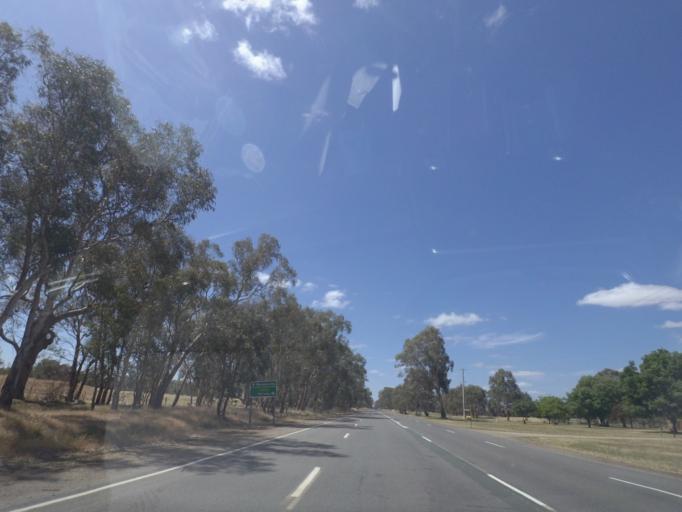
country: AU
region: Victoria
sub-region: Wangaratta
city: Wangaratta
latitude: -36.4279
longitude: 146.2558
